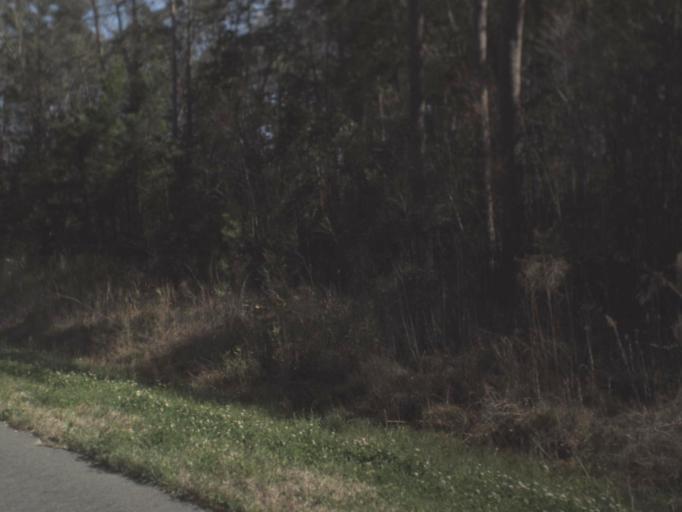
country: US
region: Florida
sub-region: Jefferson County
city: Monticello
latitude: 30.4283
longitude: -84.0198
